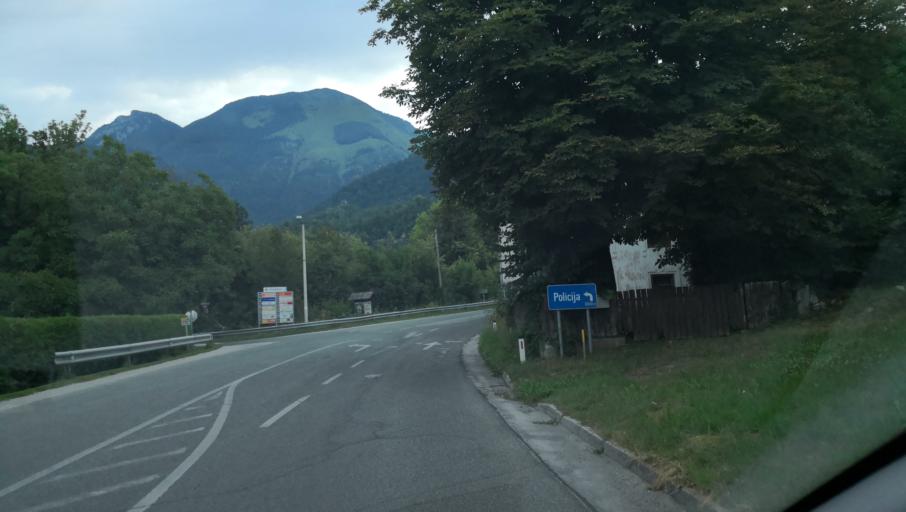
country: SI
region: Preddvor
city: Preddvor
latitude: 46.2992
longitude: 14.4289
